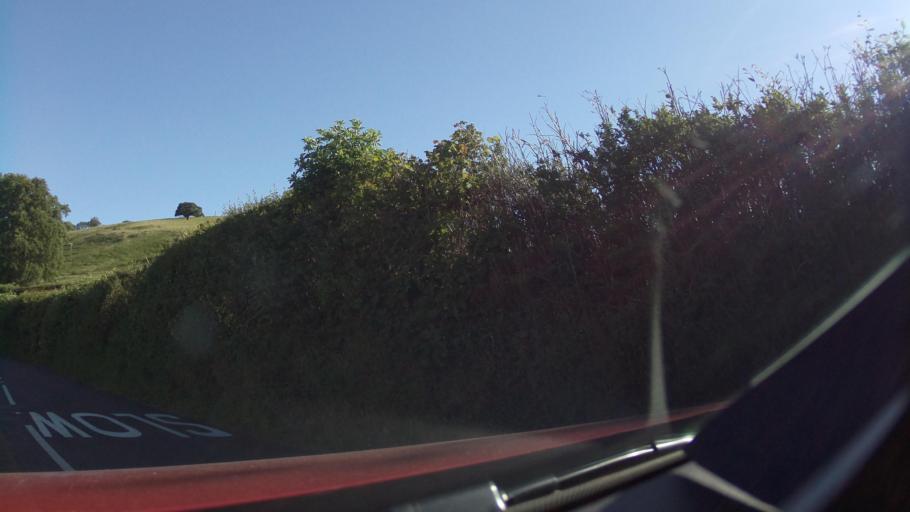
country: GB
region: England
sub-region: Somerset
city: Crewkerne
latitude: 50.8342
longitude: -2.8586
